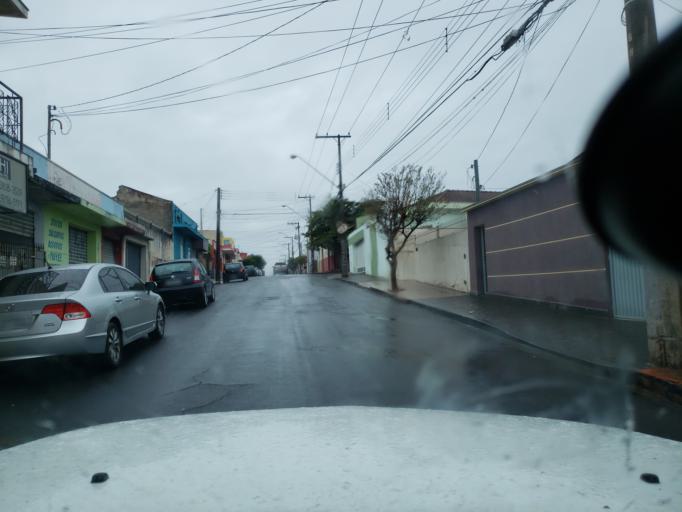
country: BR
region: Sao Paulo
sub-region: Moji-Guacu
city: Mogi-Gaucu
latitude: -22.3752
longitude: -46.9374
